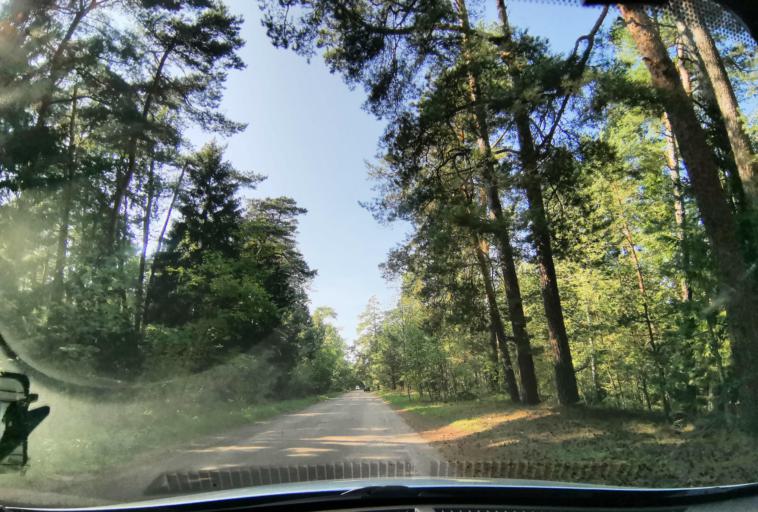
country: LT
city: Nida
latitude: 55.1611
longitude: 20.8308
